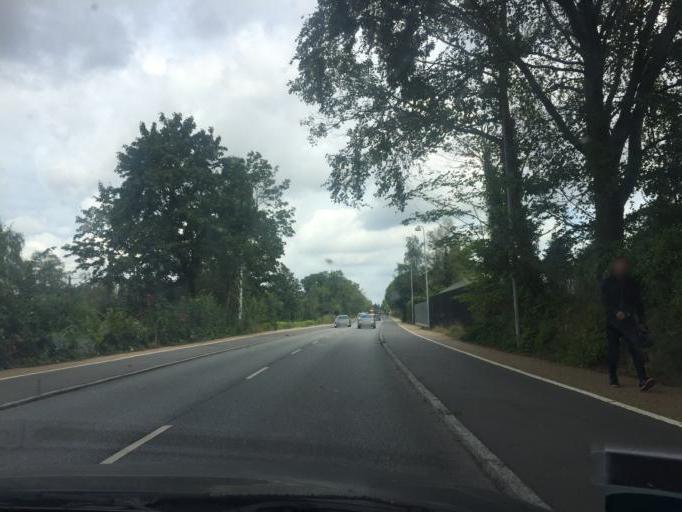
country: DK
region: Capital Region
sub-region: Allerod Kommune
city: Lillerod
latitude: 55.8739
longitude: 12.3549
